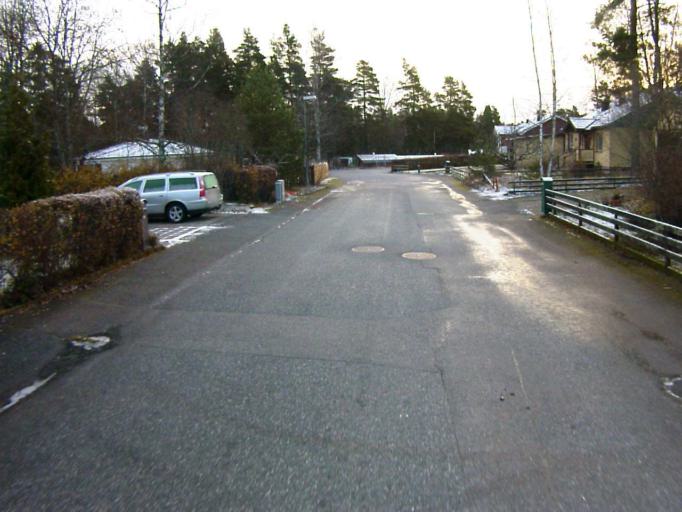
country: SE
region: Soedermanland
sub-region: Eskilstuna Kommun
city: Hallbybrunn
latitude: 59.3967
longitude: 16.4189
